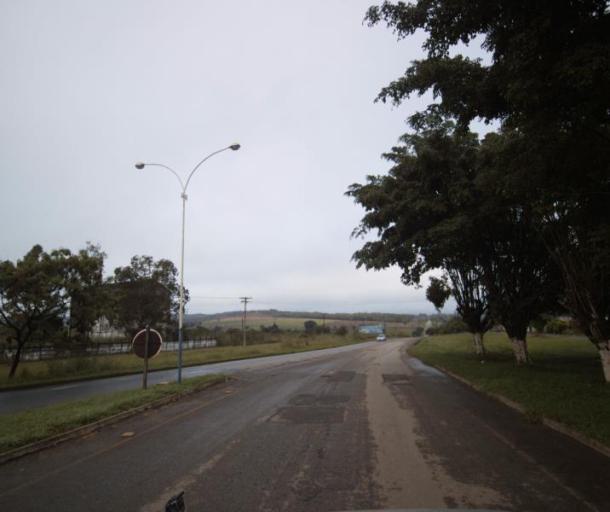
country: BR
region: Goias
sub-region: Pirenopolis
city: Pirenopolis
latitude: -15.7912
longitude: -48.7731
